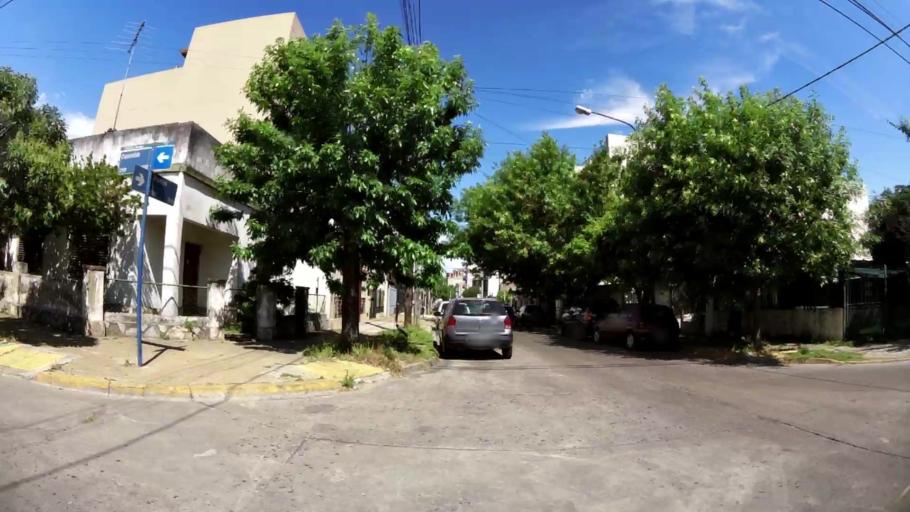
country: AR
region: Buenos Aires
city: San Justo
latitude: -34.6717
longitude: -58.5647
